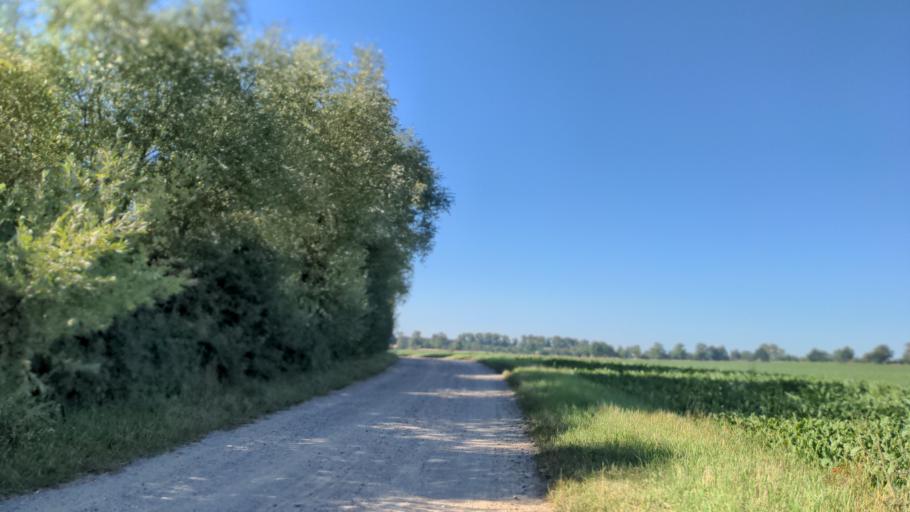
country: DE
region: Mecklenburg-Vorpommern
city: Ostseebad Boltenhagen
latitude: 53.9540
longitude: 11.2373
